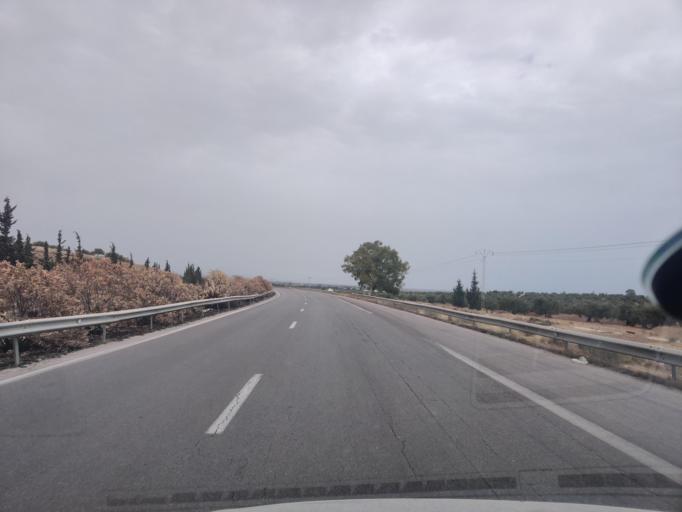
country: TN
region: Susah
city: Harqalah
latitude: 36.2396
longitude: 10.4198
